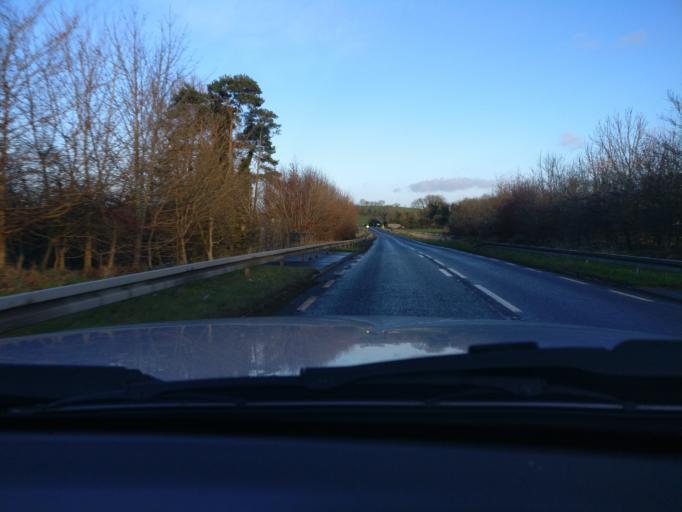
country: IE
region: Leinster
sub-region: Lu
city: Ardee
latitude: 53.8122
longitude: -6.6576
